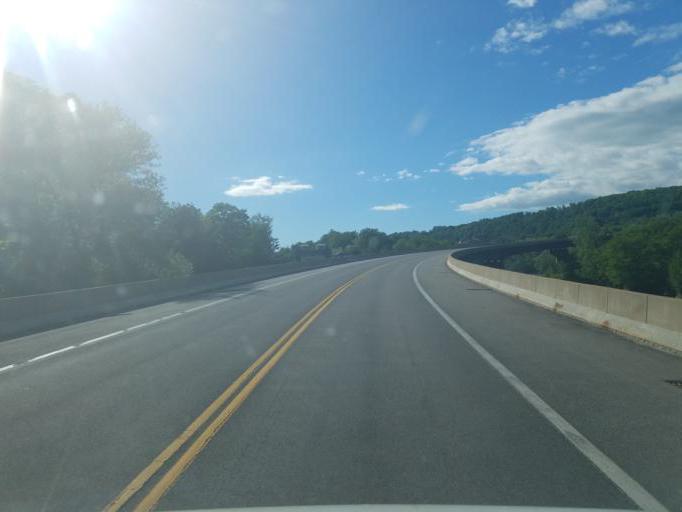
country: US
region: New York
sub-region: Herkimer County
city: Little Falls
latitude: 43.0368
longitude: -74.8432
